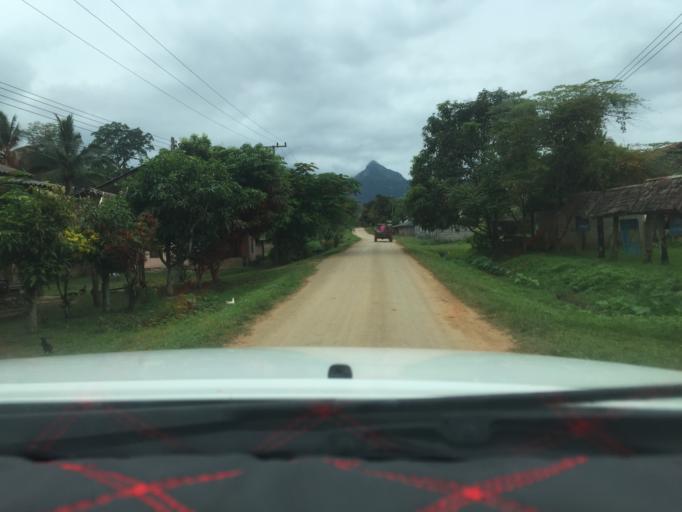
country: TH
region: Phayao
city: Phu Sang
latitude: 19.7704
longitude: 100.5431
